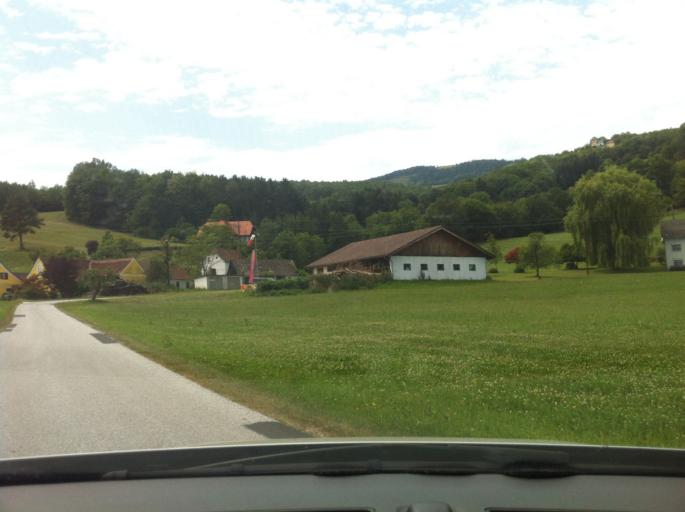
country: AT
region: Styria
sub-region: Politischer Bezirk Hartberg-Fuerstenfeld
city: Stubenberg
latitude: 47.2280
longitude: 15.7960
